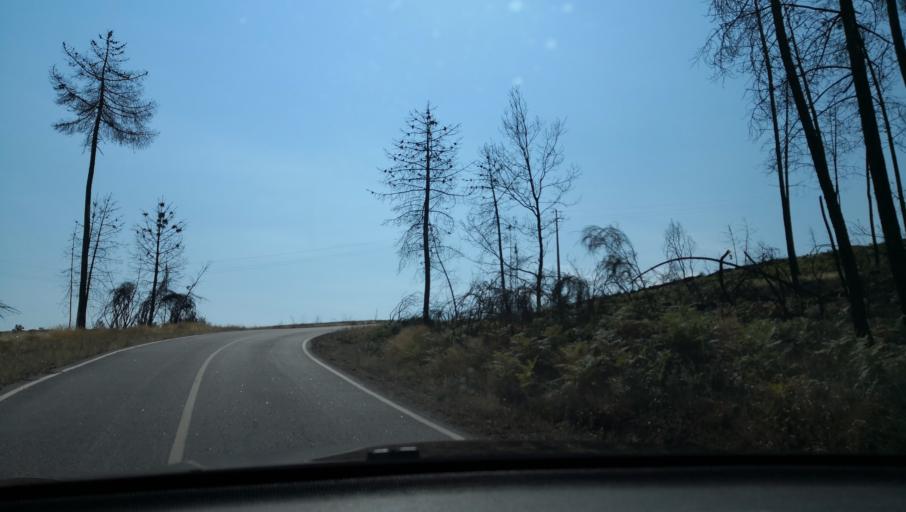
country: PT
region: Vila Real
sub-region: Sabrosa
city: Sabrosa
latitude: 41.3407
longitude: -7.5945
